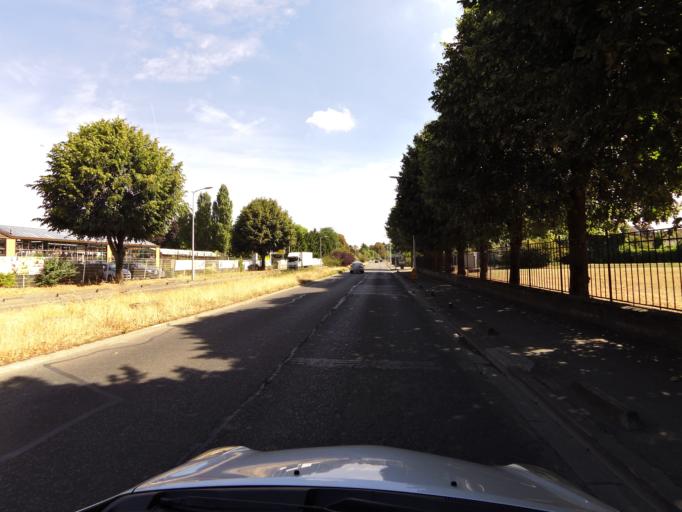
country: FR
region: Ile-de-France
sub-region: Departement de Seine-Saint-Denis
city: Neuilly-sur-Marne
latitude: 48.8617
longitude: 2.5430
